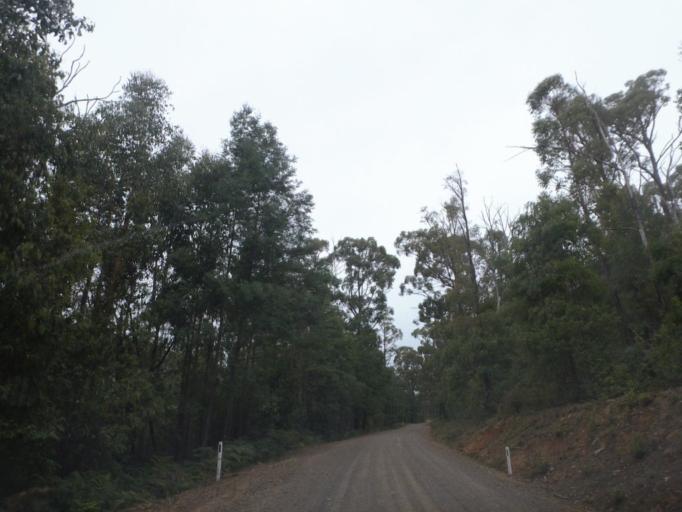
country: AU
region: Victoria
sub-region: Yarra Ranges
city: Healesville
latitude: -37.4224
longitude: 145.5789
